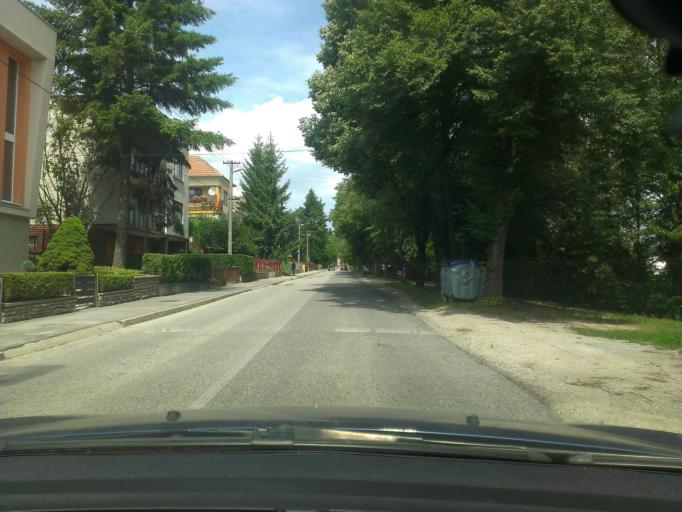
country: SK
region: Trenciansky
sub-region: Okres Myjava
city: Myjava
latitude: 48.7596
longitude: 17.5646
